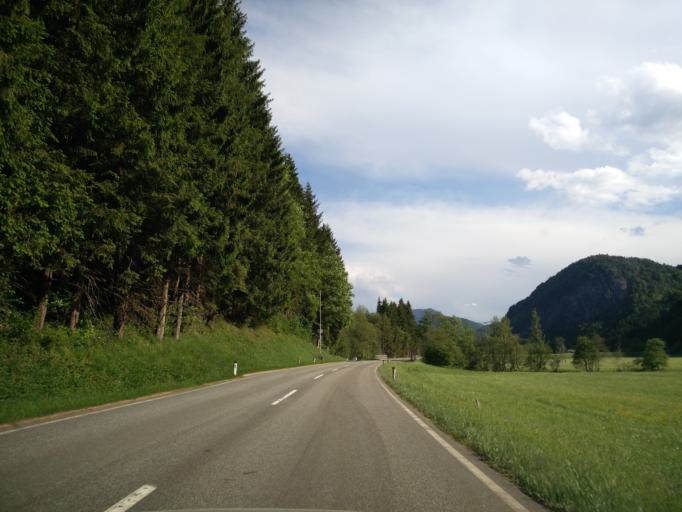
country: DE
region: Bavaria
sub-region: Upper Bavaria
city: Reit im Winkl
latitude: 47.6260
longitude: 12.4671
